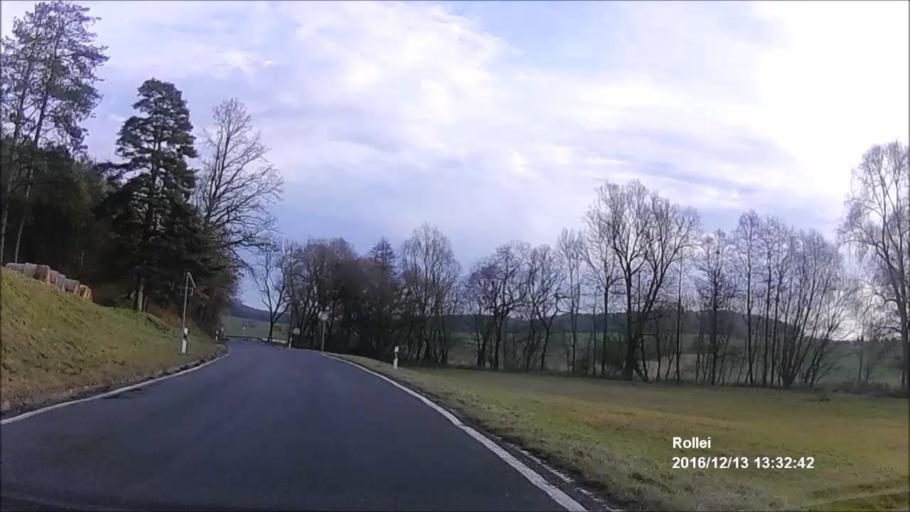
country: DE
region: Thuringia
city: Rittersdorf
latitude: 50.8517
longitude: 11.2676
